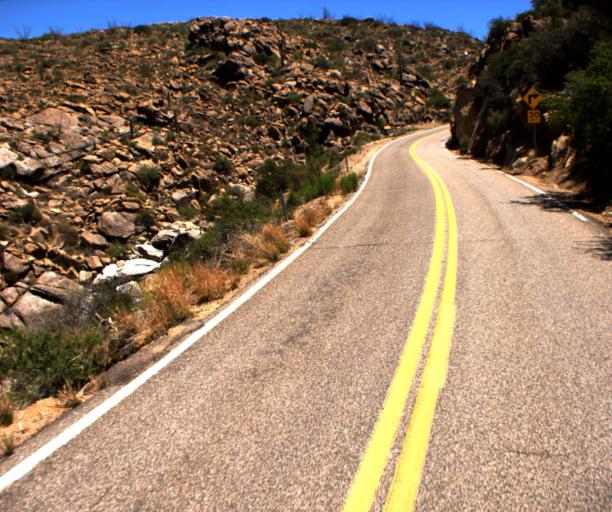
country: US
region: Arizona
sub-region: Yavapai County
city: Bagdad
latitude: 34.4498
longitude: -112.9743
